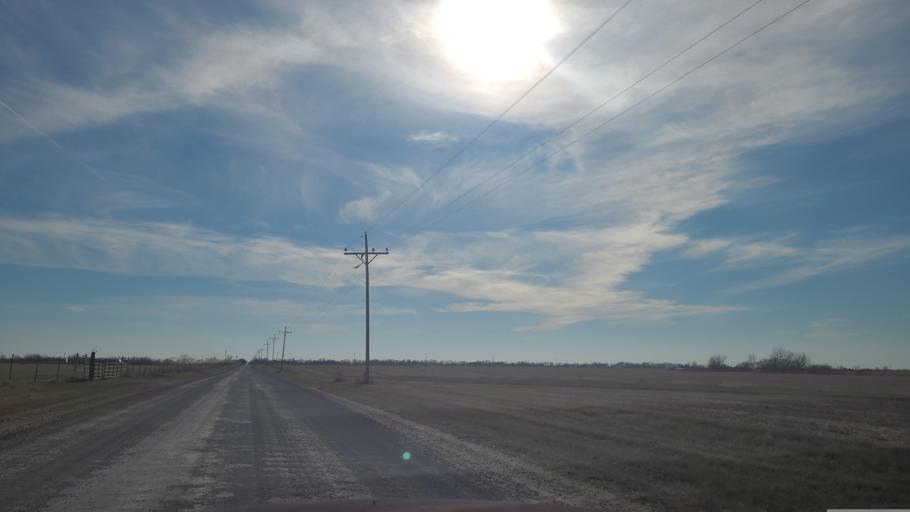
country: US
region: Kansas
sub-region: Douglas County
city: Eudora
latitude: 38.9185
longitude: -95.0748
